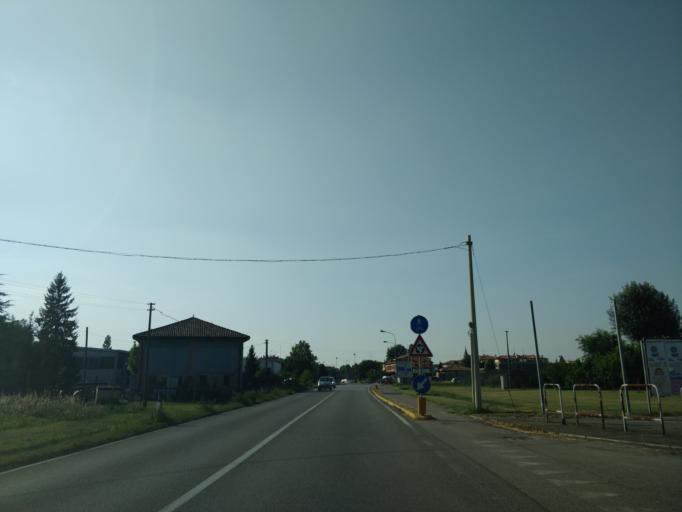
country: IT
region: Emilia-Romagna
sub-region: Provincia di Bologna
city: Castello d'Argile
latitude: 44.6745
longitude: 11.2997
